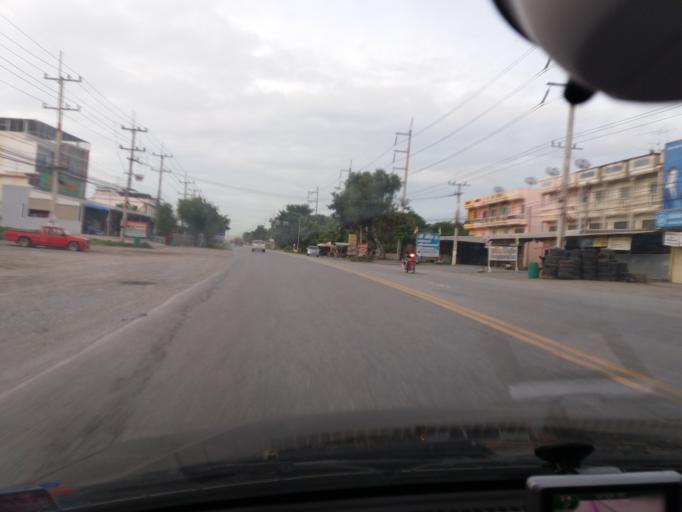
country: TH
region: Suphan Buri
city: U Thong
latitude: 14.4035
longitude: 99.8965
